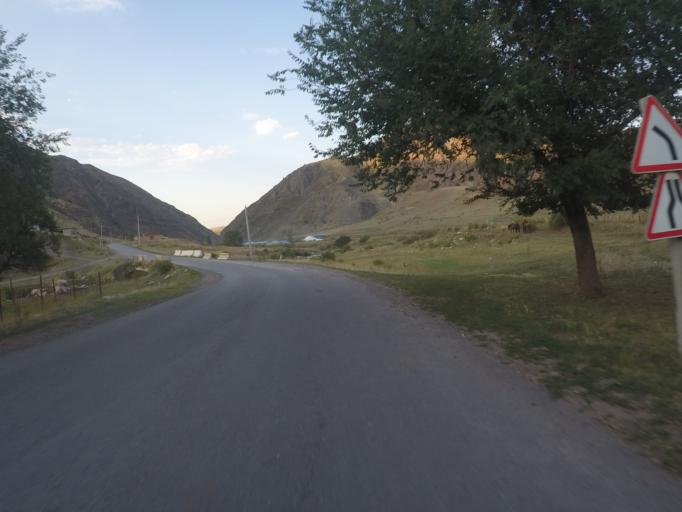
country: KG
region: Chuy
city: Bishkek
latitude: 42.6748
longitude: 74.6532
